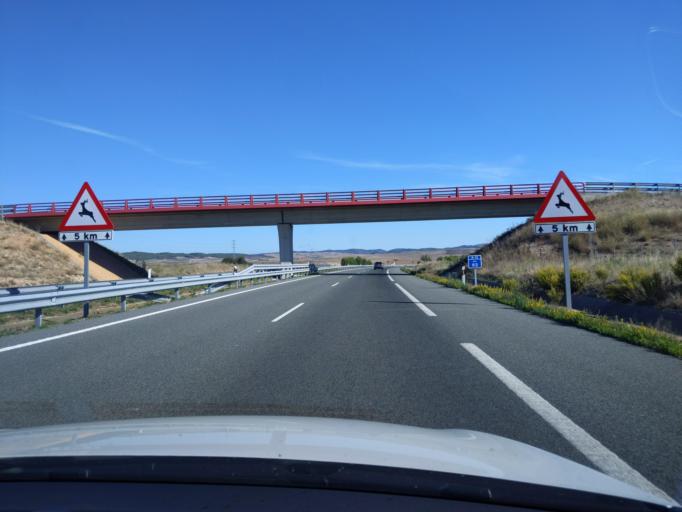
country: ES
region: Navarre
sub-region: Provincia de Navarra
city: Los Arcos
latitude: 42.5360
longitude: -2.2166
